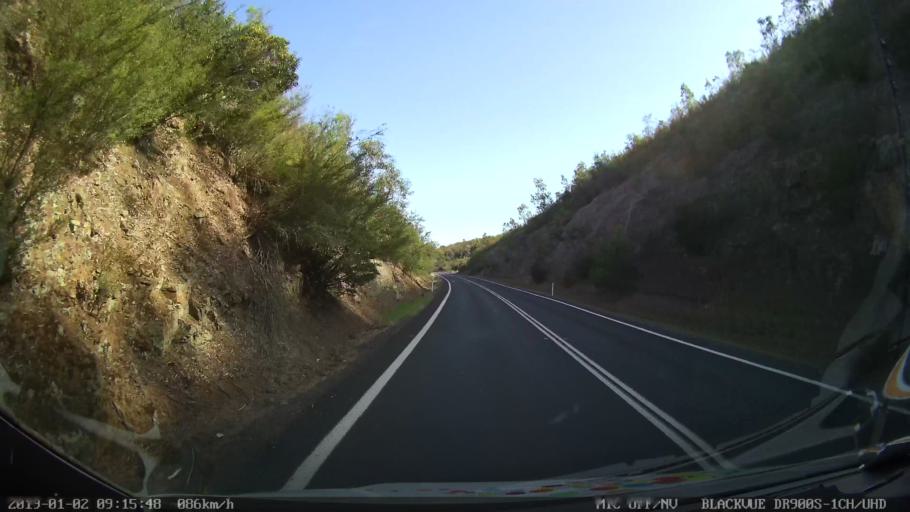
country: AU
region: New South Wales
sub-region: Tumut Shire
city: Tumut
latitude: -35.4608
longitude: 148.2818
